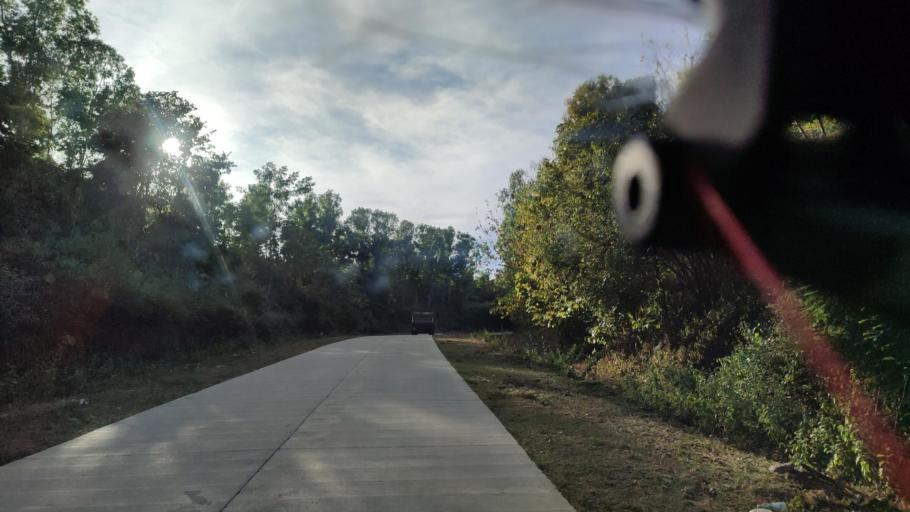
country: MM
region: Magway
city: Taungdwingyi
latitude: 20.0177
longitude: 95.7955
